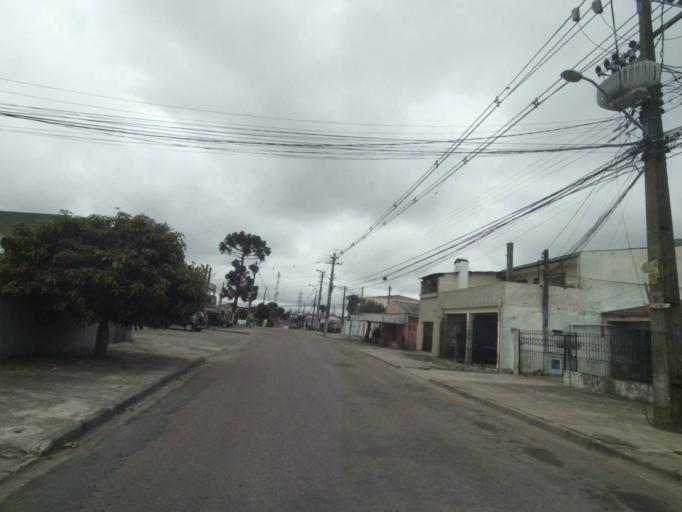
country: BR
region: Parana
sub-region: Sao Jose Dos Pinhais
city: Sao Jose dos Pinhais
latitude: -25.5406
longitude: -49.2775
